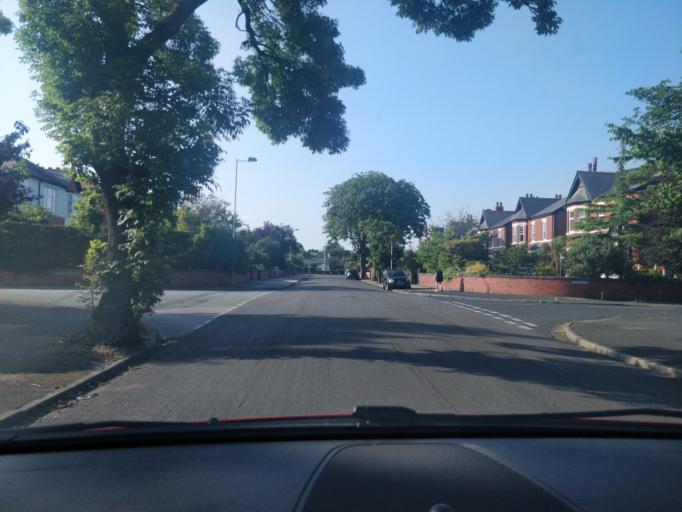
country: GB
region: England
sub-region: Sefton
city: Southport
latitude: 53.6517
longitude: -2.9742
